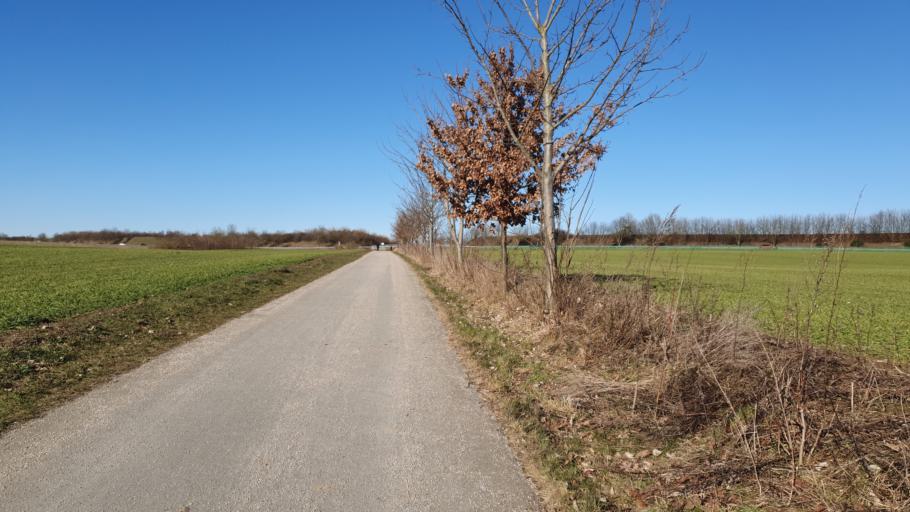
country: DE
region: Mecklenburg-Vorpommern
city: Neumuehle
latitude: 53.6308
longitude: 11.3602
